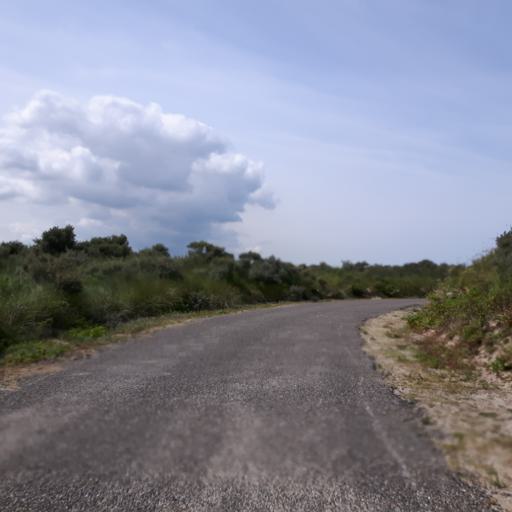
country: NL
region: Zeeland
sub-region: Gemeente Sluis
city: Sluis
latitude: 51.3883
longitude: 3.4201
